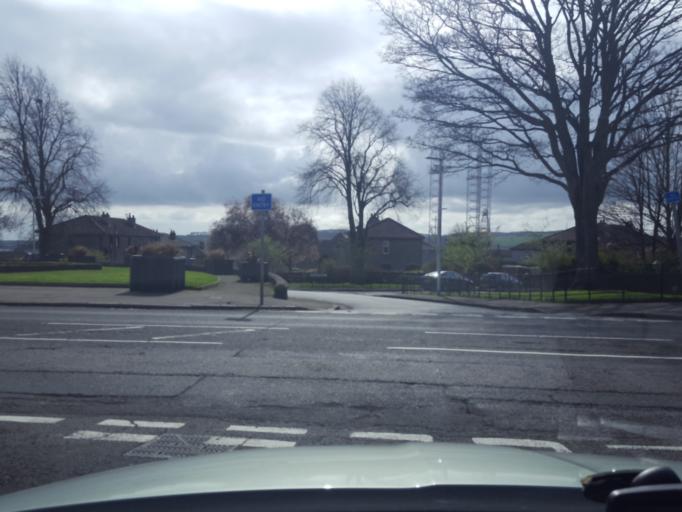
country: GB
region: Scotland
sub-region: Fife
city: Newport-On-Tay
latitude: 56.4730
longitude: -2.9300
